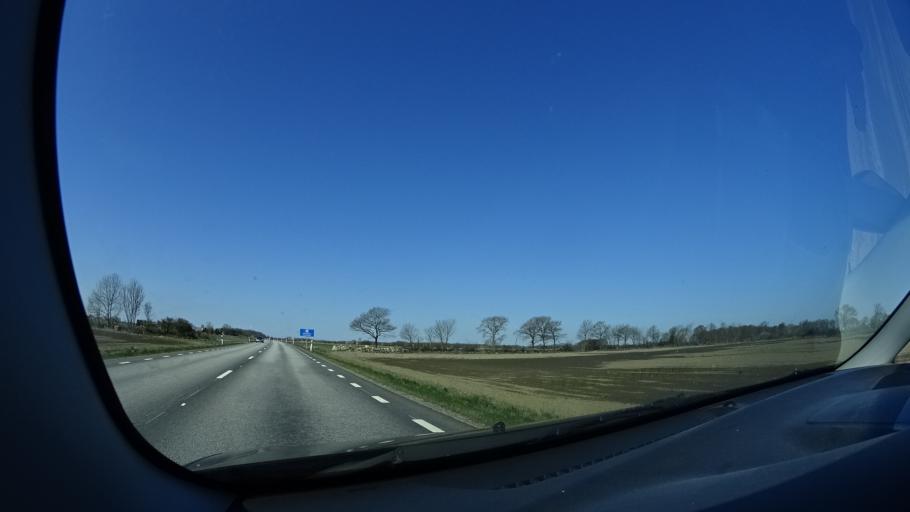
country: SE
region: Skane
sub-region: Angelholms Kommun
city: Strovelstorp
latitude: 56.2078
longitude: 12.7462
